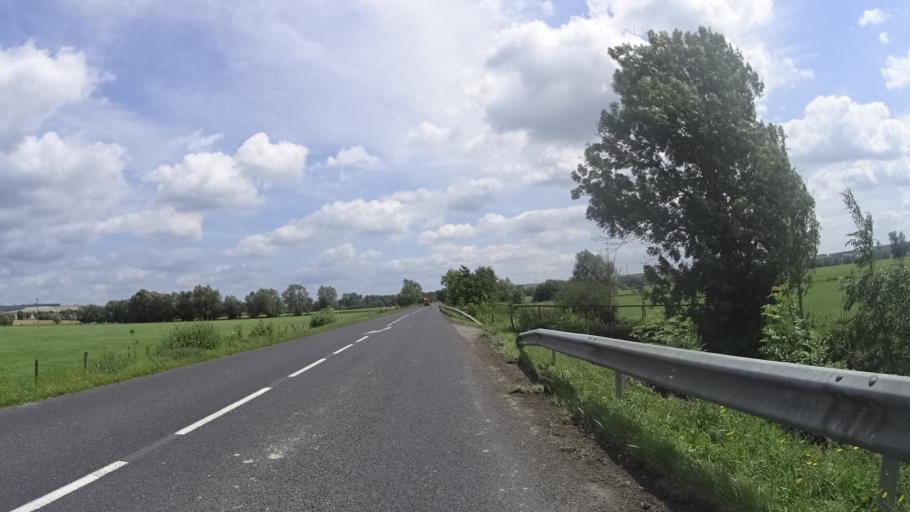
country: FR
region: Lorraine
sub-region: Departement de la Meuse
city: Euville
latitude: 48.7149
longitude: 5.6724
